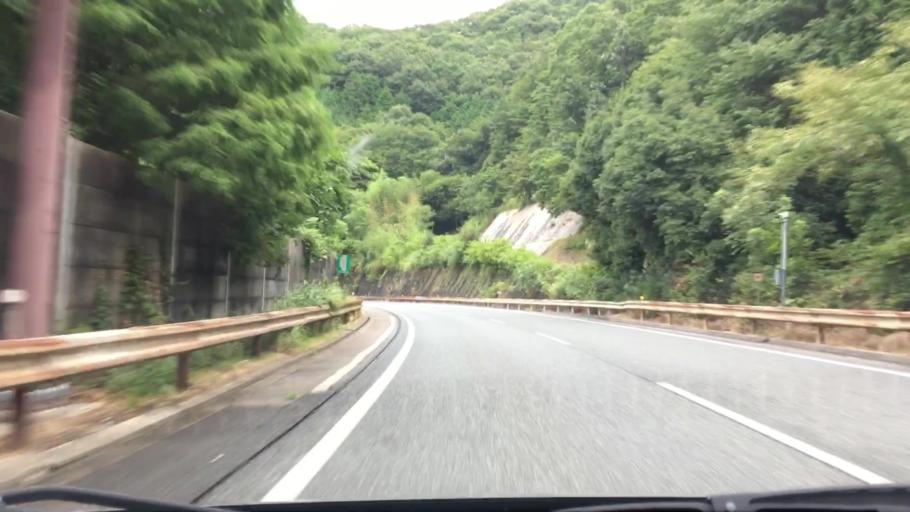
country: JP
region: Okayama
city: Niimi
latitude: 34.9926
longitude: 133.4586
